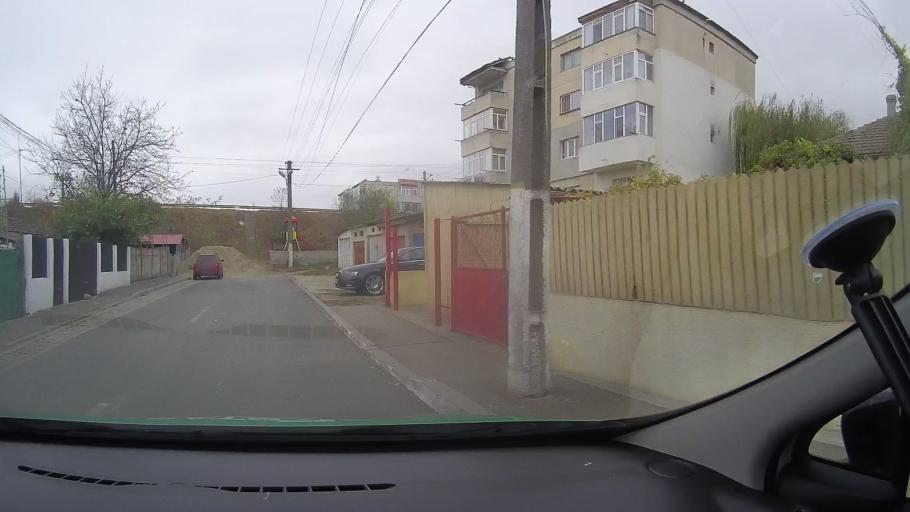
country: RO
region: Constanta
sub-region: Oras Murfatlar
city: Murfatlar
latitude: 44.1730
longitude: 28.4112
